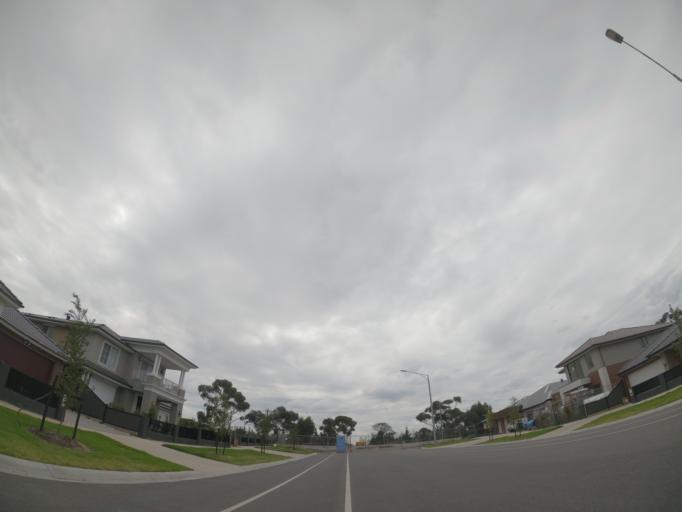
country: AU
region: Victoria
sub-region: Hume
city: Craigieburn
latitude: -37.5651
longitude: 144.8964
